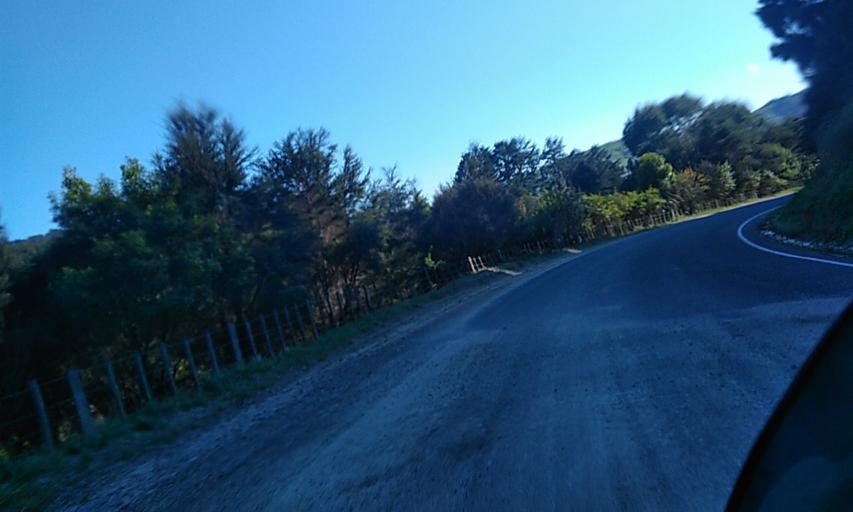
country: NZ
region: Gisborne
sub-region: Gisborne District
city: Gisborne
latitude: -38.5242
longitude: 178.0337
